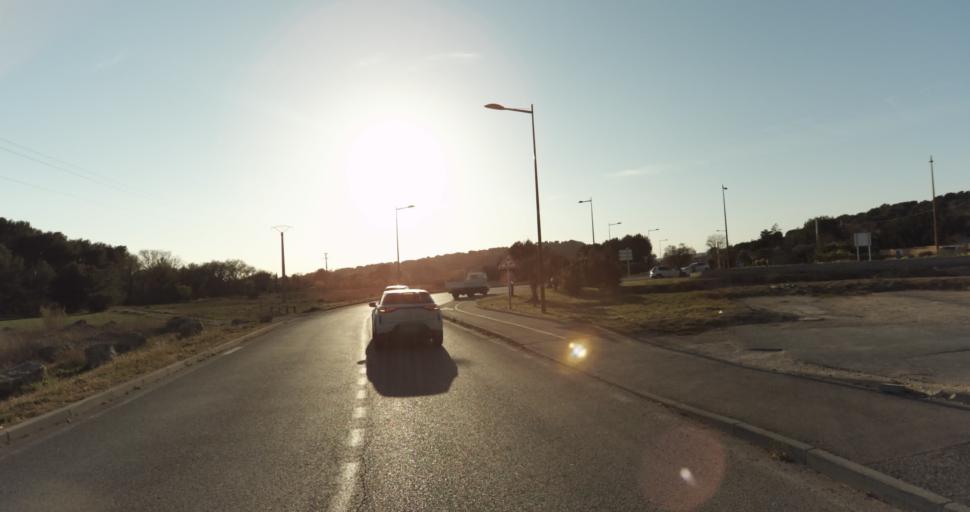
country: FR
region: Provence-Alpes-Cote d'Azur
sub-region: Departement des Bouches-du-Rhone
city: Velaux
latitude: 43.5398
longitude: 5.2679
